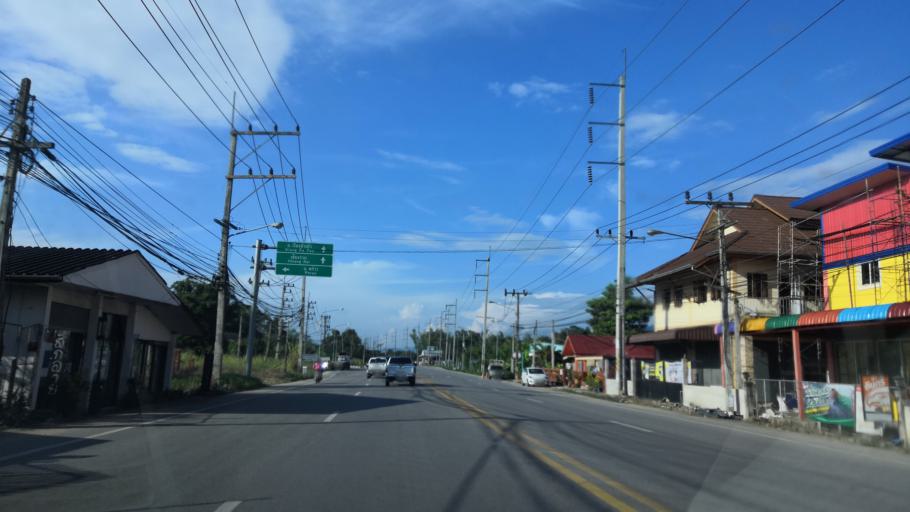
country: TH
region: Chiang Rai
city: Wiang Pa Pao
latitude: 19.3230
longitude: 99.5127
